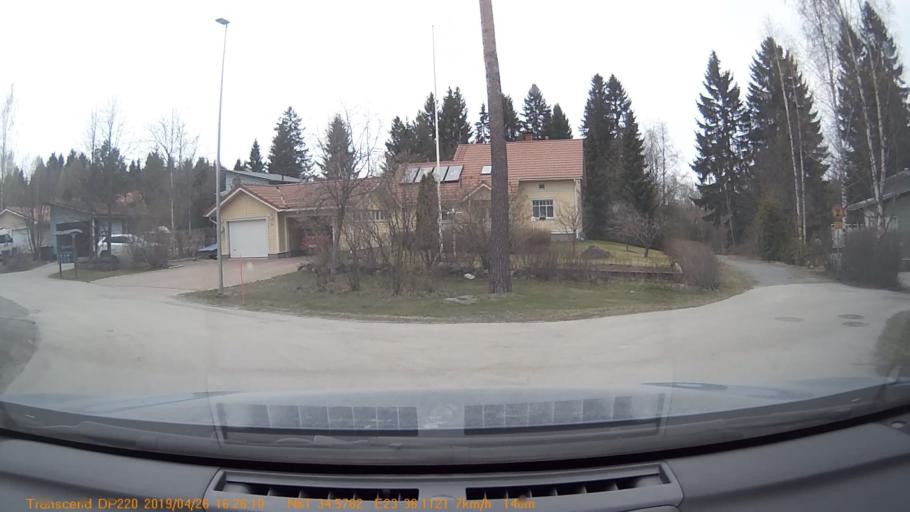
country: FI
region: Pirkanmaa
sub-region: Tampere
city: Yloejaervi
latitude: 61.5762
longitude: 23.6017
